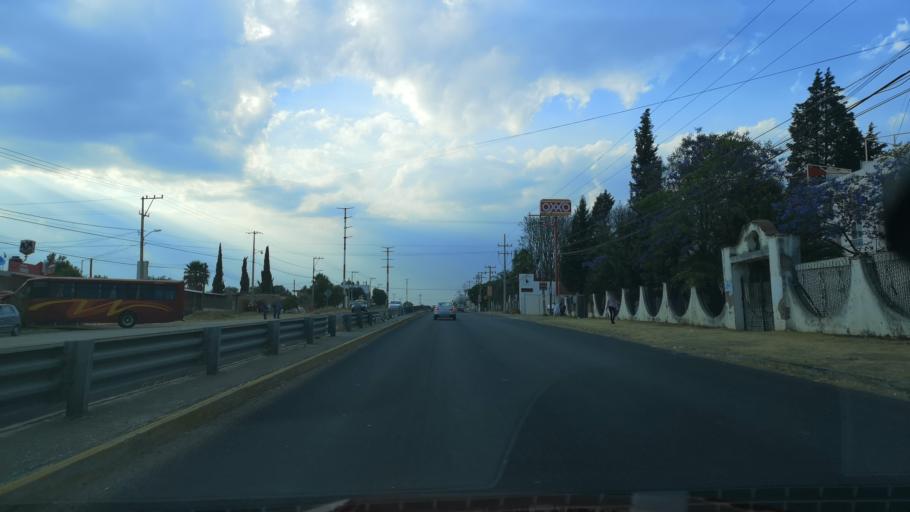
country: MX
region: Puebla
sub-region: Juan C. Bonilla
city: Santa Maria Zacatepec
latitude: 19.1114
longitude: -98.3549
